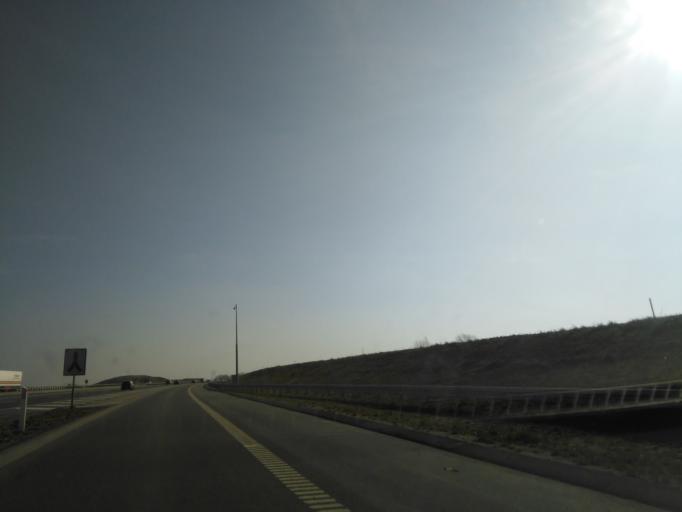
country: DK
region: South Denmark
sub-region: Middelfart Kommune
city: Norre Aby
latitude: 55.4765
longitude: 9.8850
